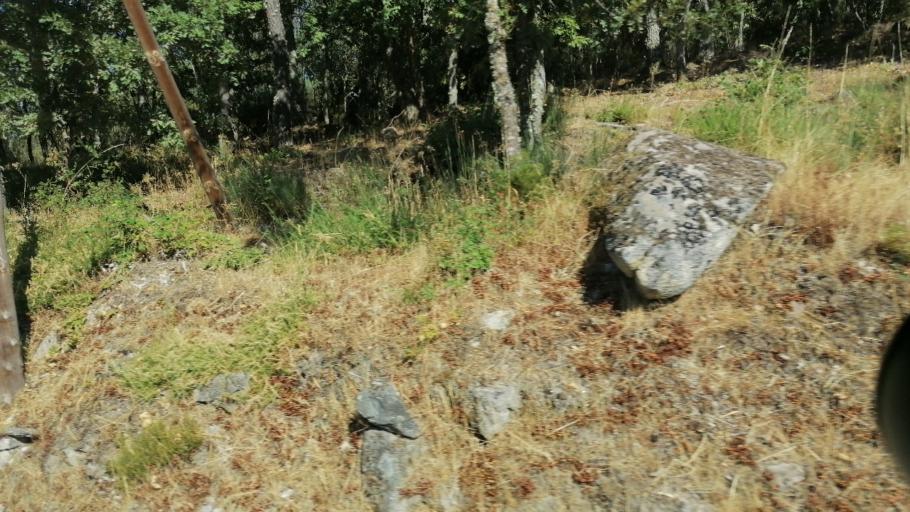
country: PT
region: Vila Real
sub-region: Sabrosa
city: Sabrosa
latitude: 41.3714
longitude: -7.5629
